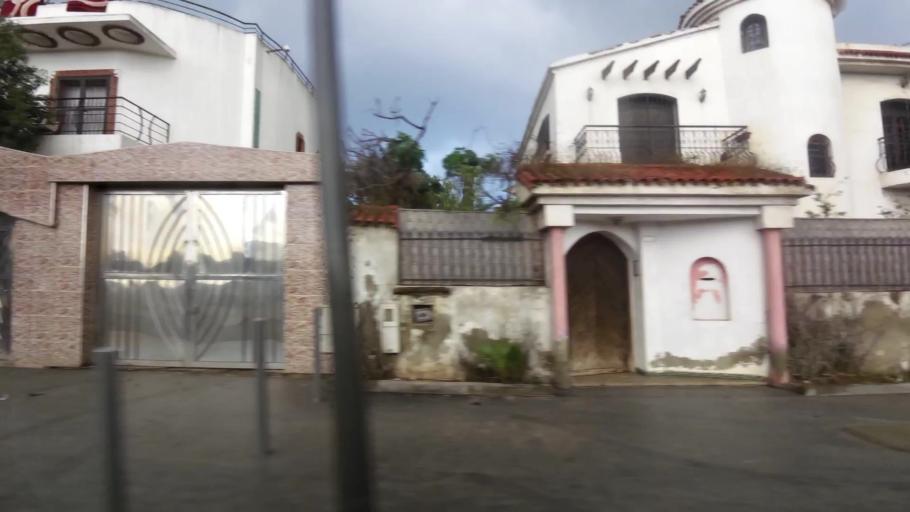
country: MA
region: Grand Casablanca
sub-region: Casablanca
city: Casablanca
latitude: 33.5446
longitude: -7.6627
